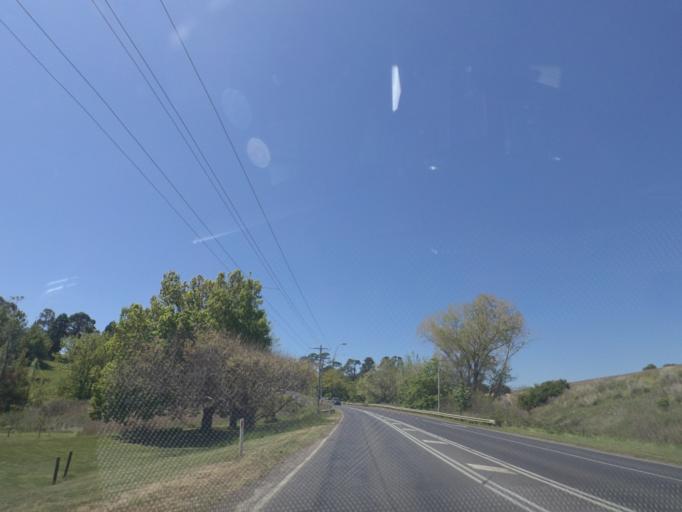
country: AU
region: Victoria
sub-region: Hume
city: Sunbury
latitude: -37.4655
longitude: 144.6723
